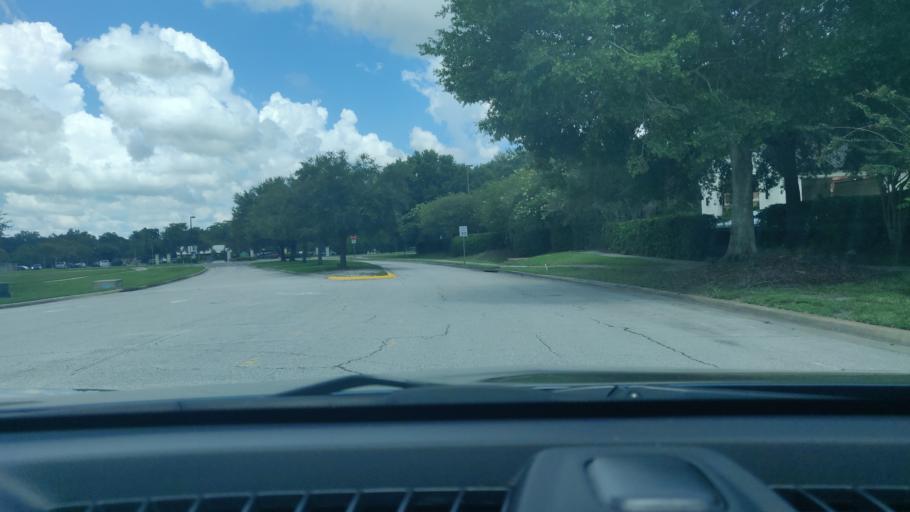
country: US
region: Florida
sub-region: Orange County
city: Conway
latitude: 28.4605
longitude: -81.3134
